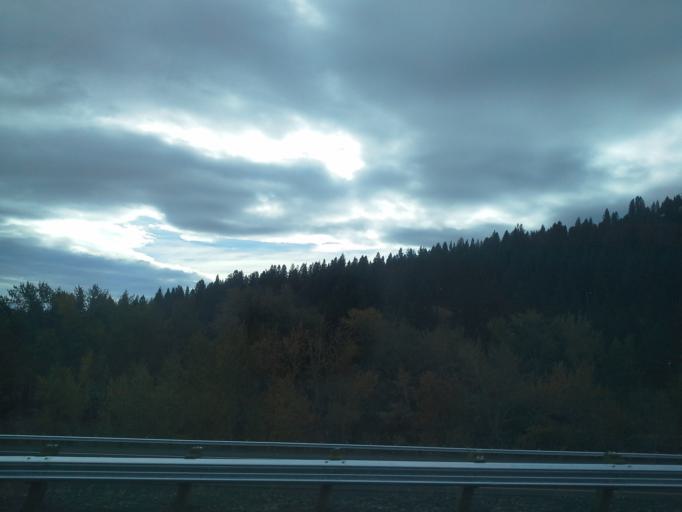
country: US
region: Oregon
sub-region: Union County
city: La Grande
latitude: 45.3433
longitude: -118.1151
